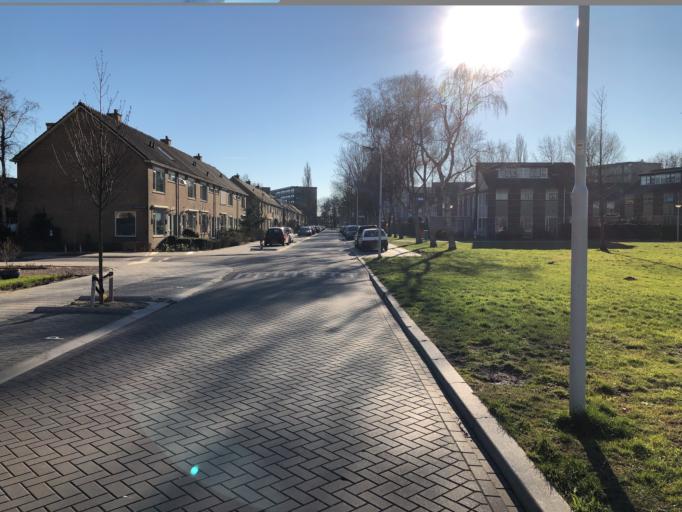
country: NL
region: North Holland
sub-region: Gemeente Uitgeest
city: Uitgeest
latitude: 52.5075
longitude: 4.7535
